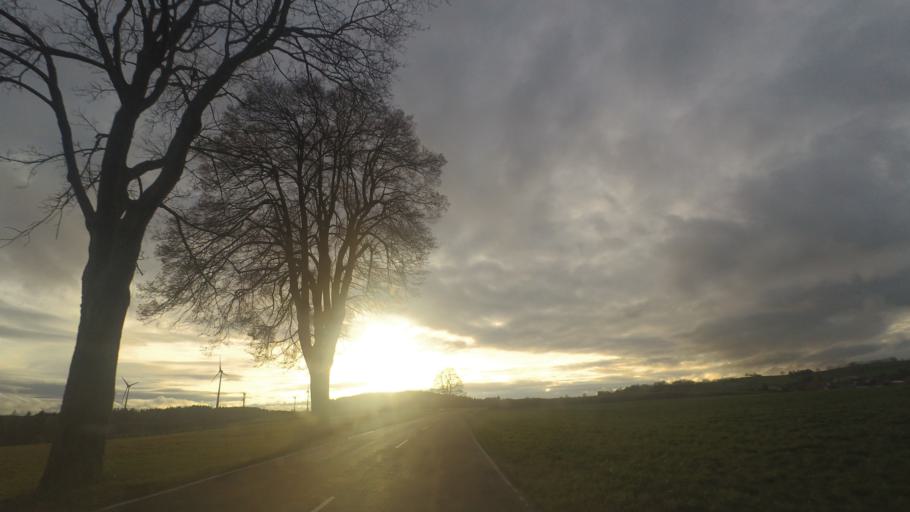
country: DE
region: Hesse
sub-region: Regierungsbezirk Giessen
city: Freiensteinau
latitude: 50.4599
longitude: 9.4174
